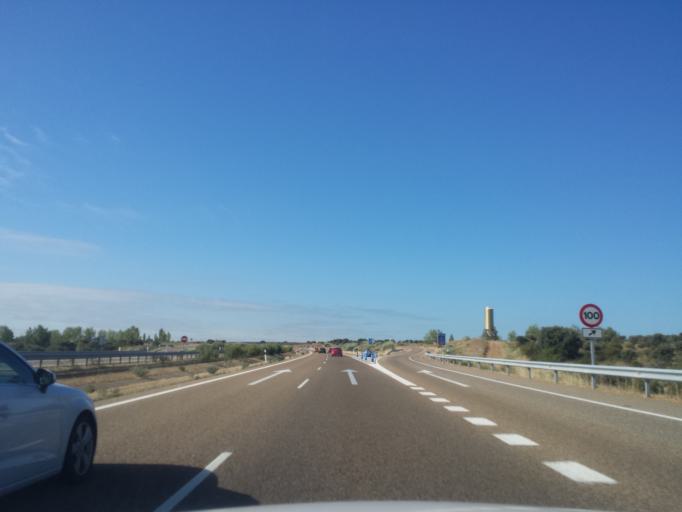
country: ES
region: Castille and Leon
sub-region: Provincia de Leon
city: Valdevimbre
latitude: 42.4023
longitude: -5.5938
